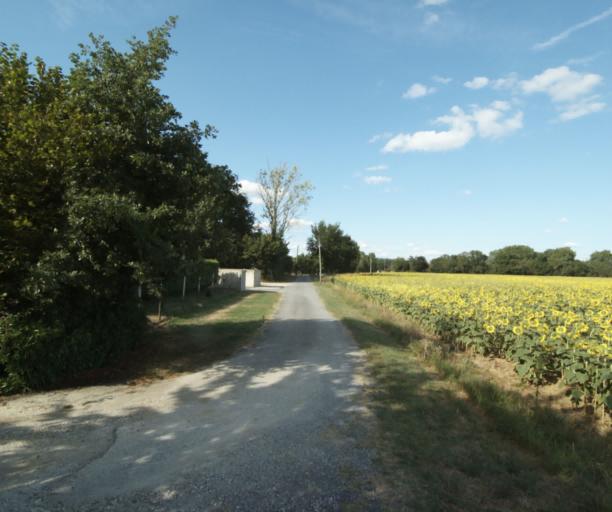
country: FR
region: Midi-Pyrenees
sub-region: Departement du Tarn
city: Puylaurens
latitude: 43.5161
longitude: 1.9981
